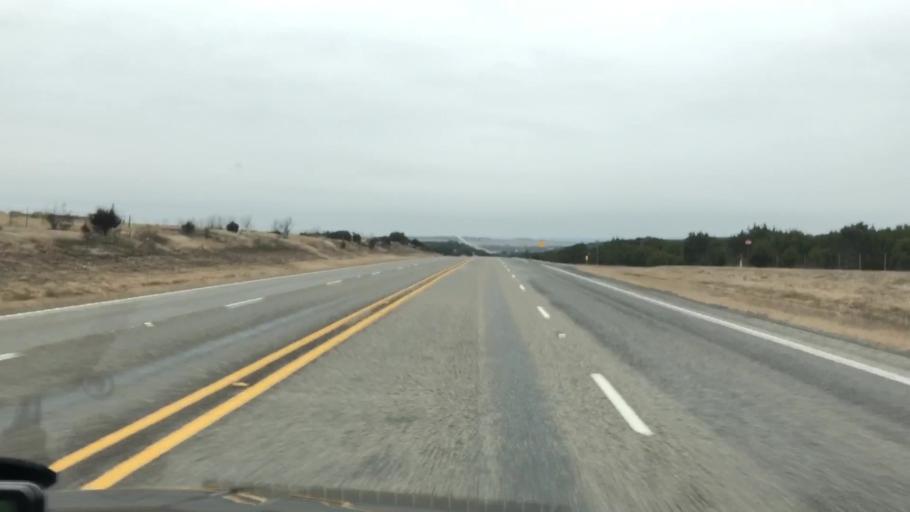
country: US
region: Texas
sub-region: Lampasas County
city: Lampasas
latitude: 31.1941
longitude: -98.1720
